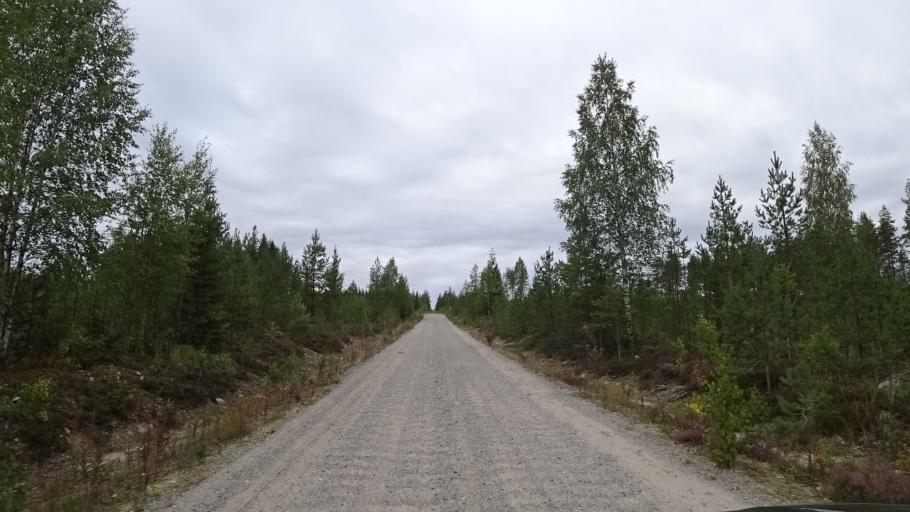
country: FI
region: North Karelia
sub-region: Joensuu
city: Ilomantsi
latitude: 63.1555
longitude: 30.6300
